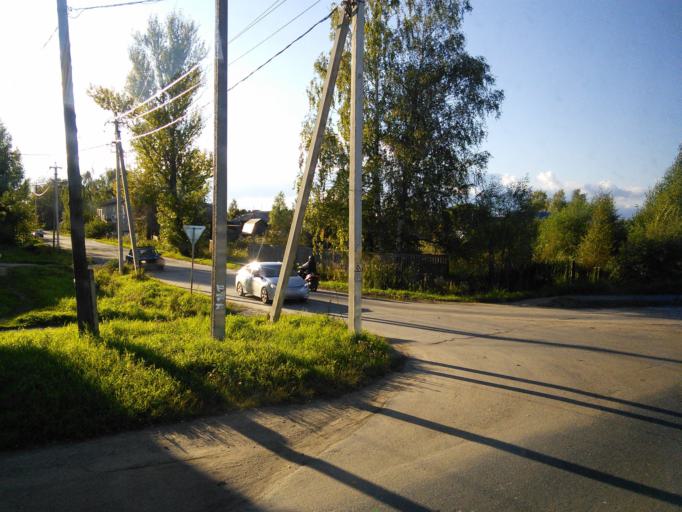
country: RU
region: Jaroslavl
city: Poshekhon'ye
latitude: 58.5036
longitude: 39.1305
